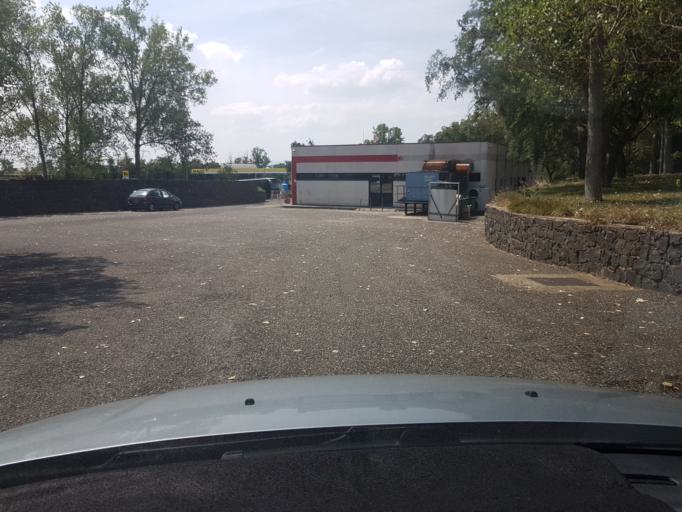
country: IT
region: Sardinia
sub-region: Provincia di Oristano
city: Abbasanta
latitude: 40.1106
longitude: 8.7919
